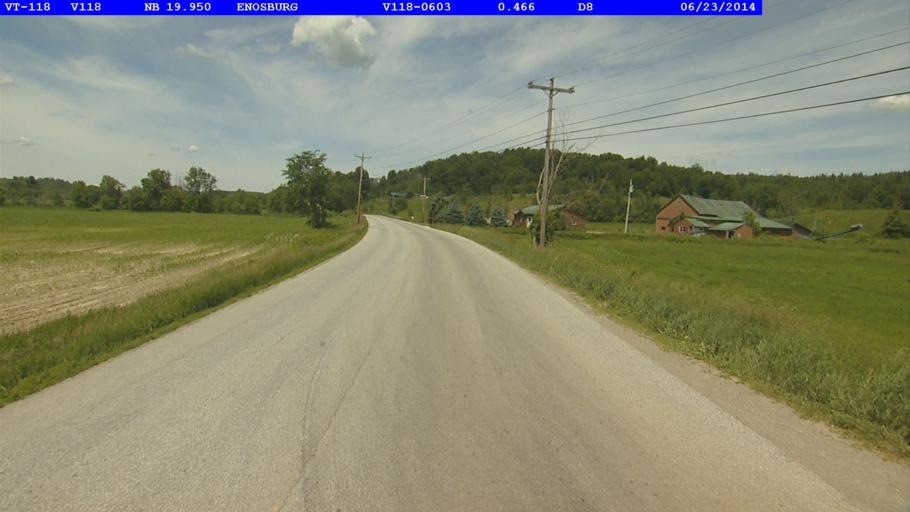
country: US
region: Vermont
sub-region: Franklin County
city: Richford
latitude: 44.9264
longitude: -72.6780
